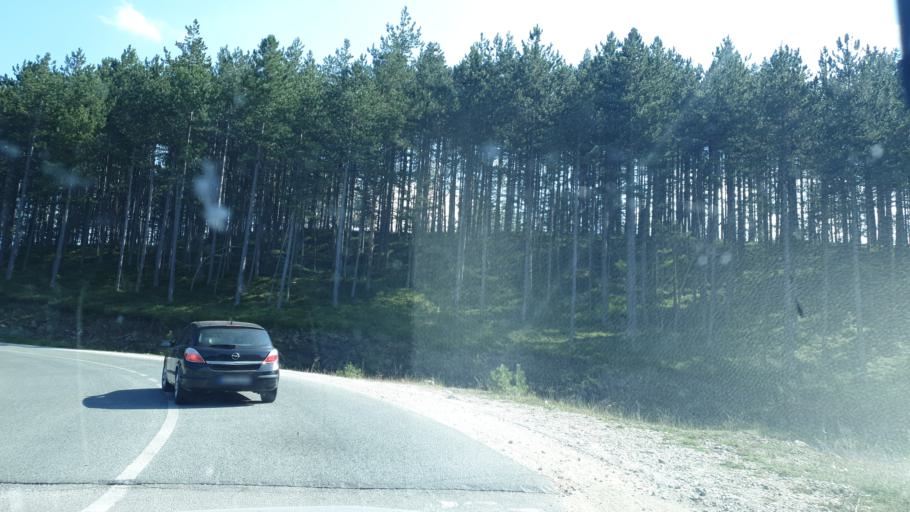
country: RS
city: Zlatibor
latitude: 43.6904
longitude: 19.6623
